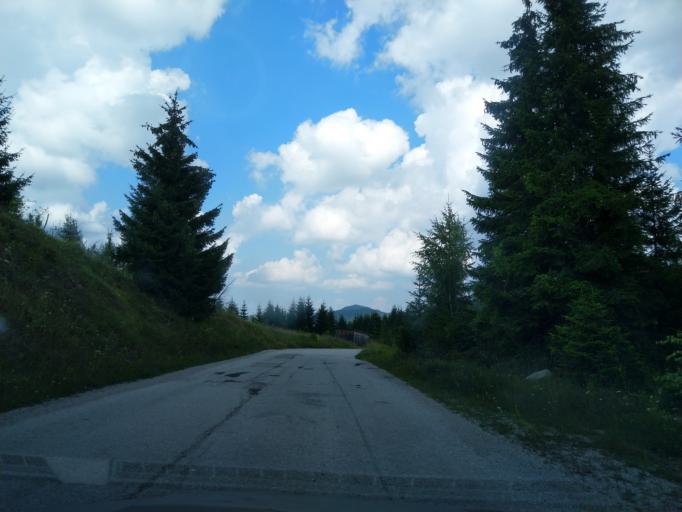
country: RS
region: Central Serbia
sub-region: Zlatiborski Okrug
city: Nova Varos
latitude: 43.5258
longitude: 19.8763
